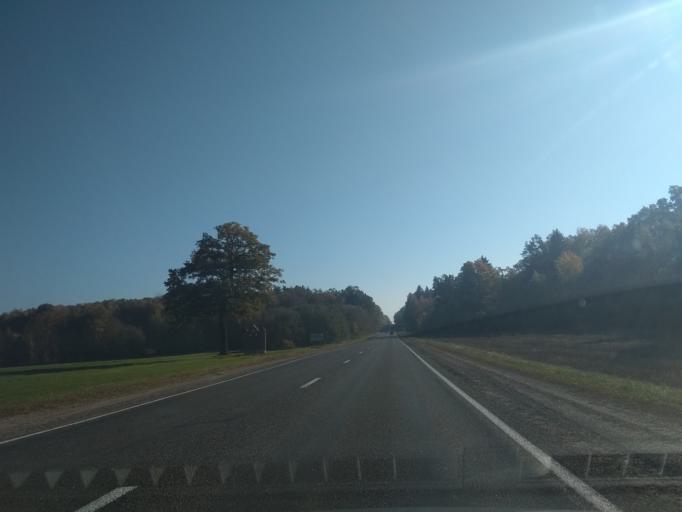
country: BY
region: Grodnenskaya
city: Slonim
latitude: 53.1120
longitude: 25.1621
